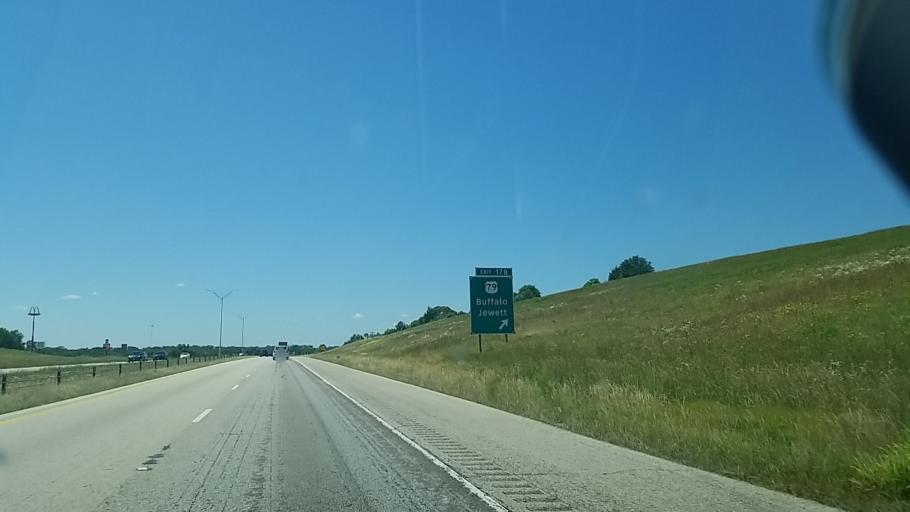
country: US
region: Texas
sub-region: Leon County
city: Buffalo
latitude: 31.4457
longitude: -96.0711
